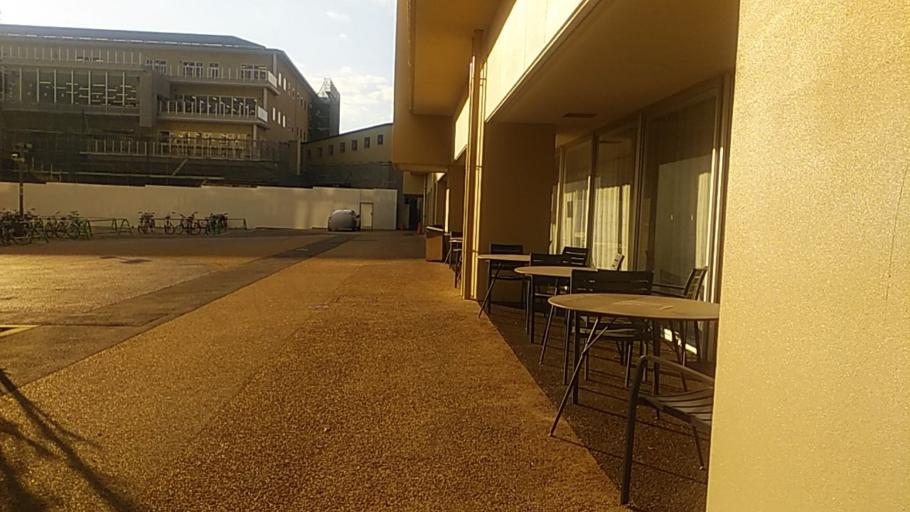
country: JP
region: Kyoto
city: Kyoto
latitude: 35.0102
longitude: 135.7189
